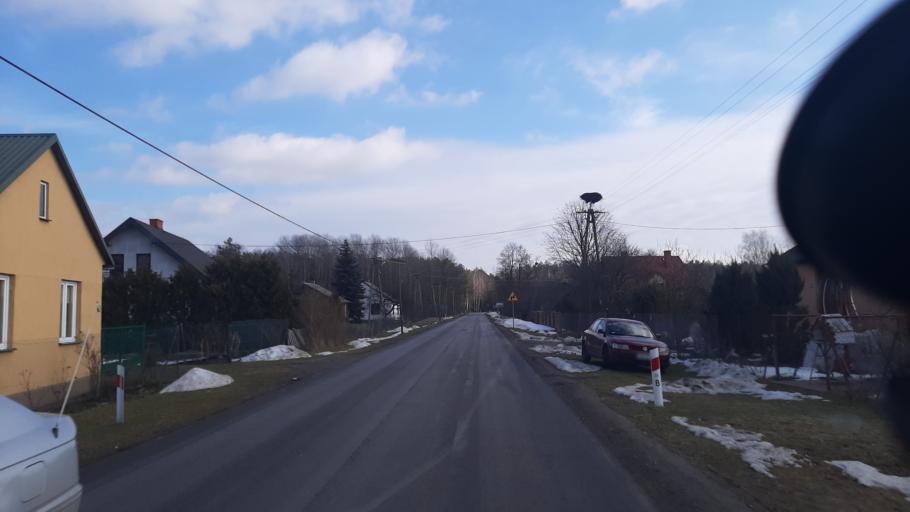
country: PL
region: Lublin Voivodeship
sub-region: Powiat wlodawski
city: Urszulin
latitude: 51.4967
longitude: 23.2622
